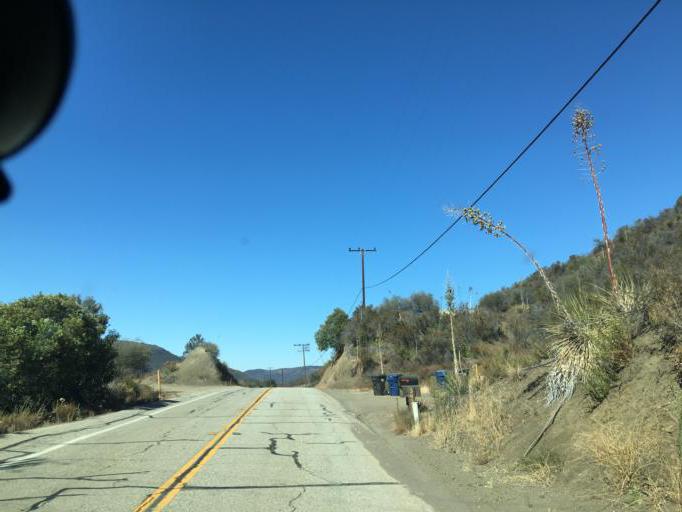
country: US
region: California
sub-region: Ventura County
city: Thousand Oaks
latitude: 34.0887
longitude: -118.8942
